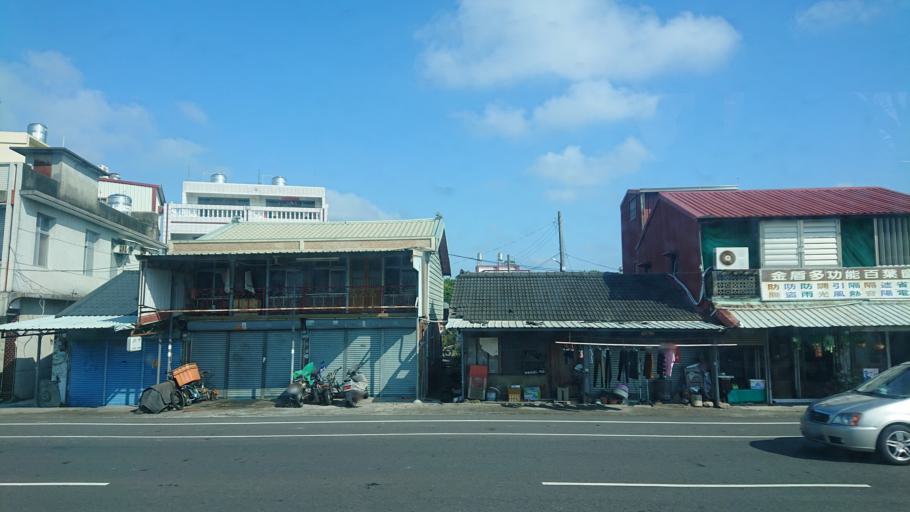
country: TW
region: Taiwan
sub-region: Chiayi
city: Taibao
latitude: 23.4572
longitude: 120.3116
